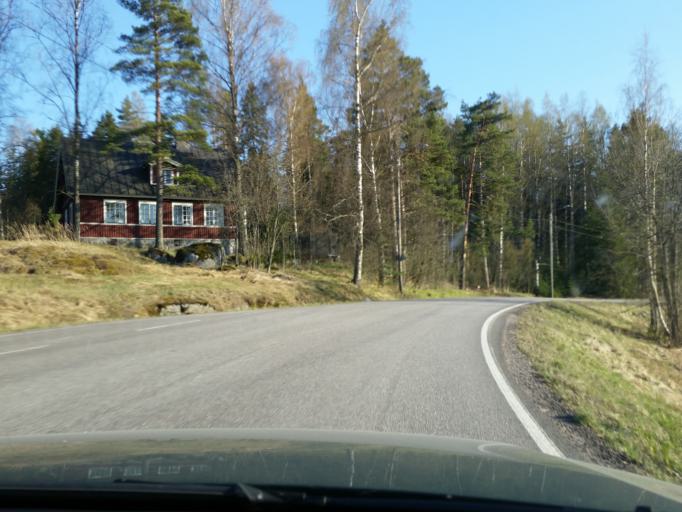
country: FI
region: Uusimaa
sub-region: Helsinki
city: Espoo
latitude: 60.1099
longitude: 24.5695
